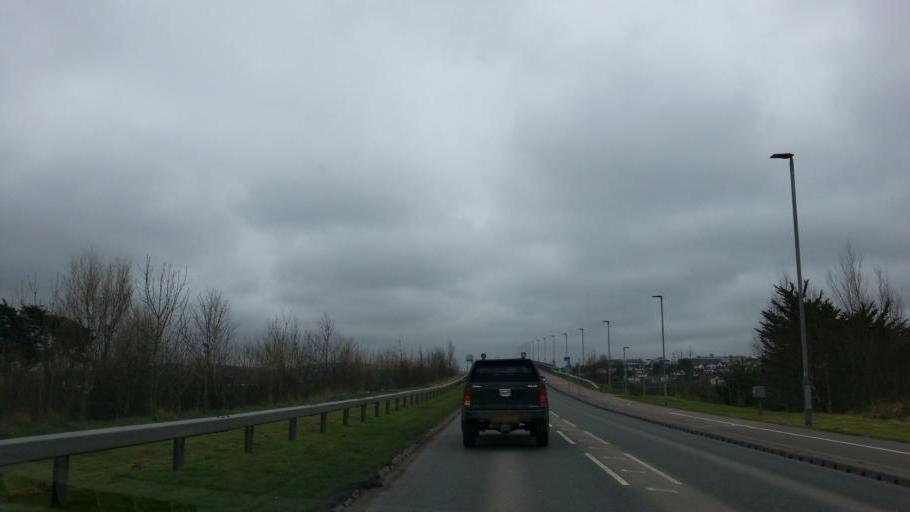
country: GB
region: England
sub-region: Devon
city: Barnstaple
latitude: 51.0823
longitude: -4.0732
